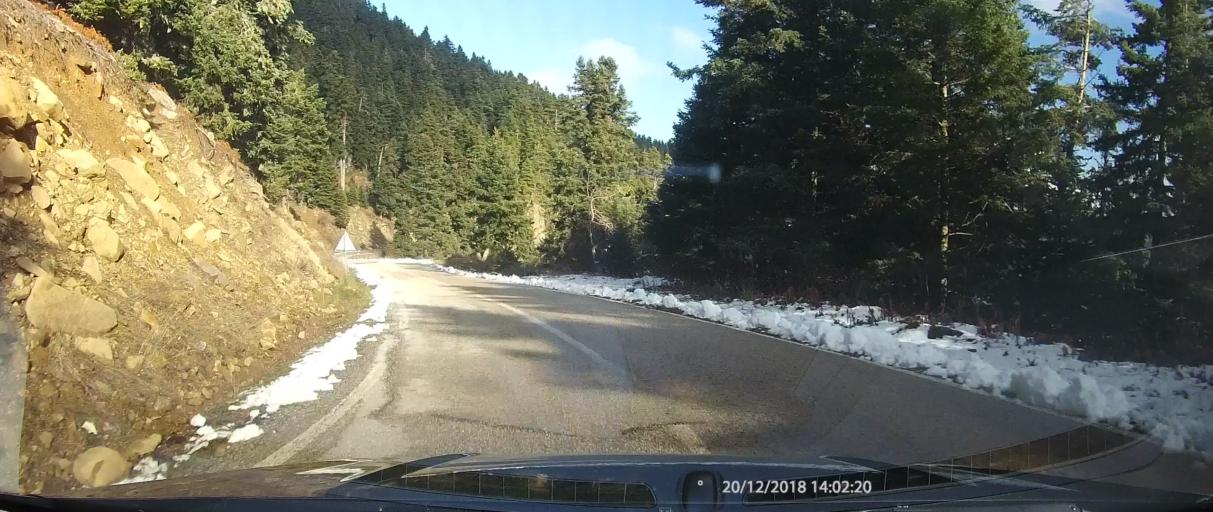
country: GR
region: West Greece
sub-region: Nomos Aitolias kai Akarnanias
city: Thermo
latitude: 38.7369
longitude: 21.6353
